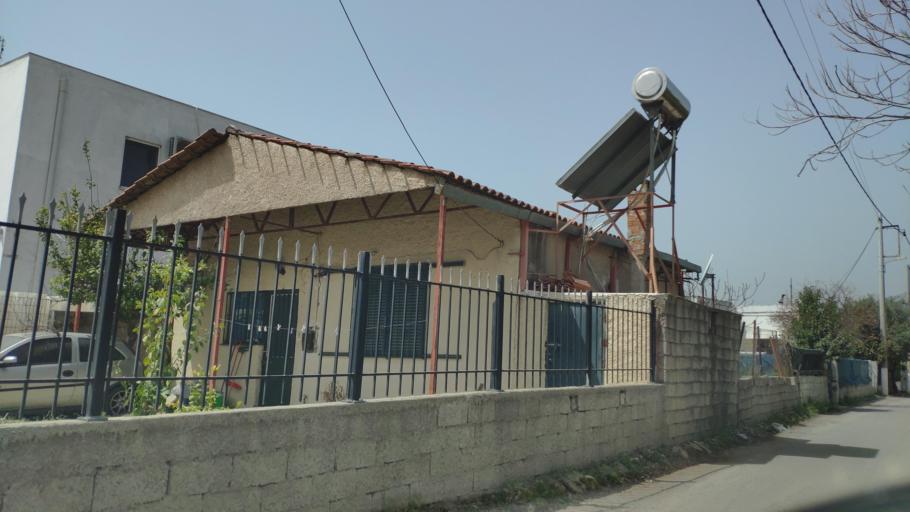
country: GR
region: Attica
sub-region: Nomarchia Athinas
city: Metamorfosi
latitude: 38.0725
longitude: 23.7629
